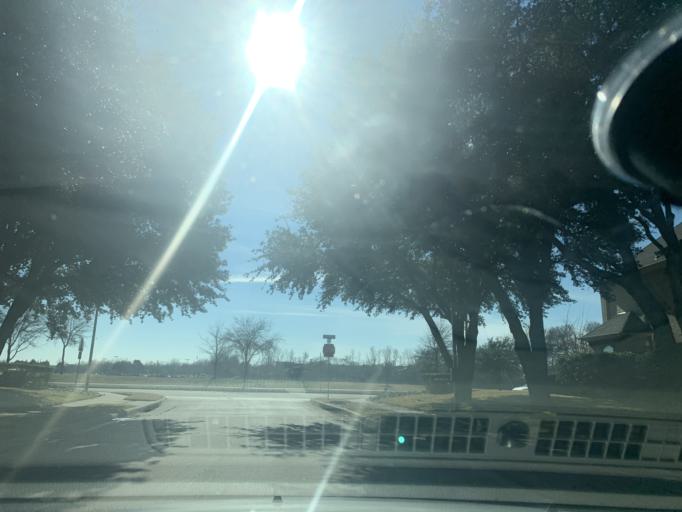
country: US
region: Texas
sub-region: Denton County
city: The Colony
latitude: 33.0503
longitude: -96.8204
